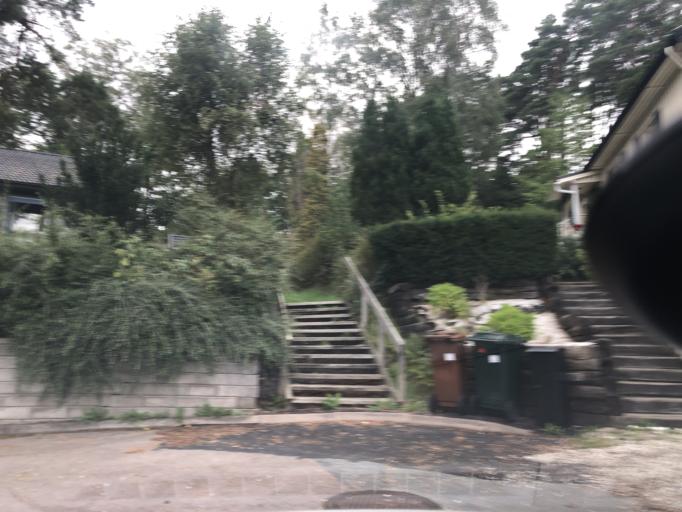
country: SE
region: Vaestra Goetaland
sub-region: Goteborg
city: Goeteborg
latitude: 57.7570
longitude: 11.9589
